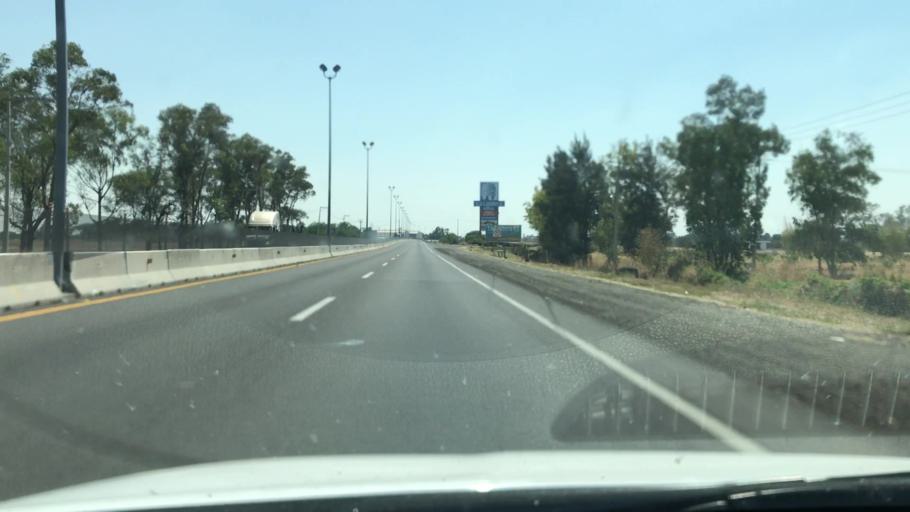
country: MX
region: Guanajuato
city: Abasolo
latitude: 20.4616
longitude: -101.5249
